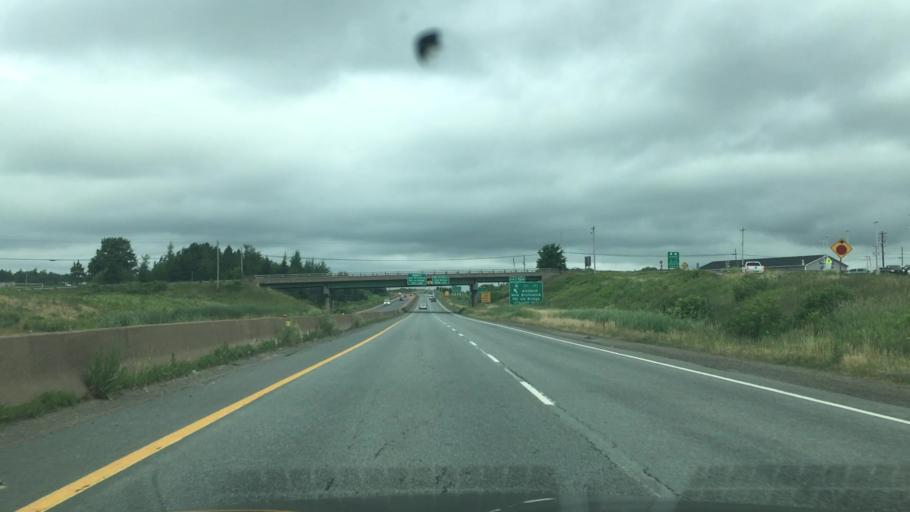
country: CA
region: Nova Scotia
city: Truro
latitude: 45.3790
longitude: -63.3206
